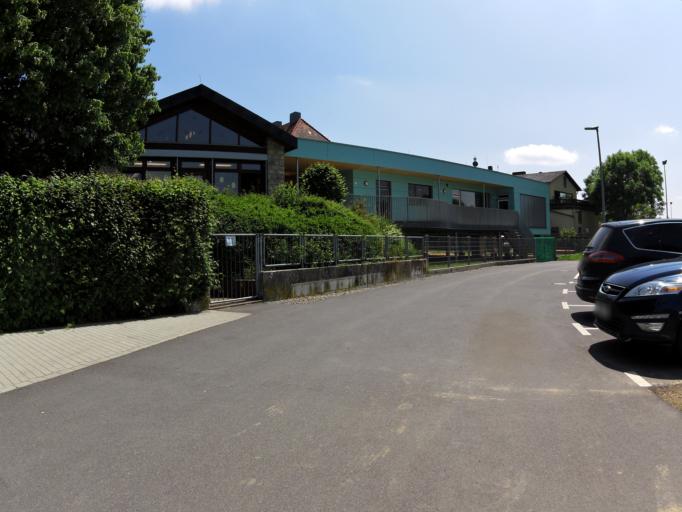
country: DE
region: Bavaria
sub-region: Regierungsbezirk Unterfranken
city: Kleinrinderfeld
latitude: 49.6987
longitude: 9.8422
